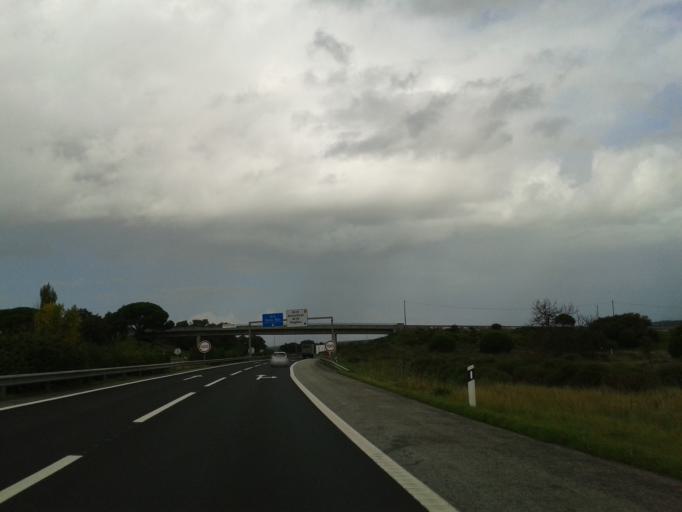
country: PT
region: Setubal
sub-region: Alcochete
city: Alcochete
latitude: 38.7368
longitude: -8.9341
